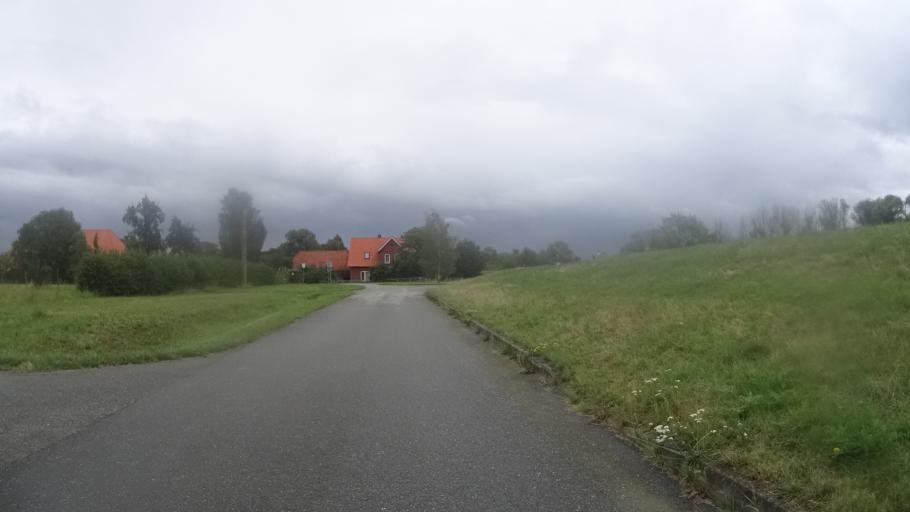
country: DE
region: Lower Saxony
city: Tosterglope
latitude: 53.2588
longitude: 10.8348
